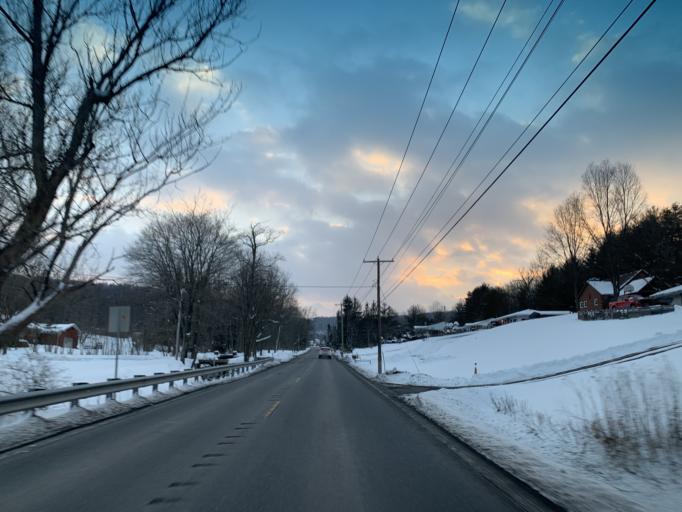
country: US
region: Maryland
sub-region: Allegany County
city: Frostburg
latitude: 39.6734
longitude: -78.9043
